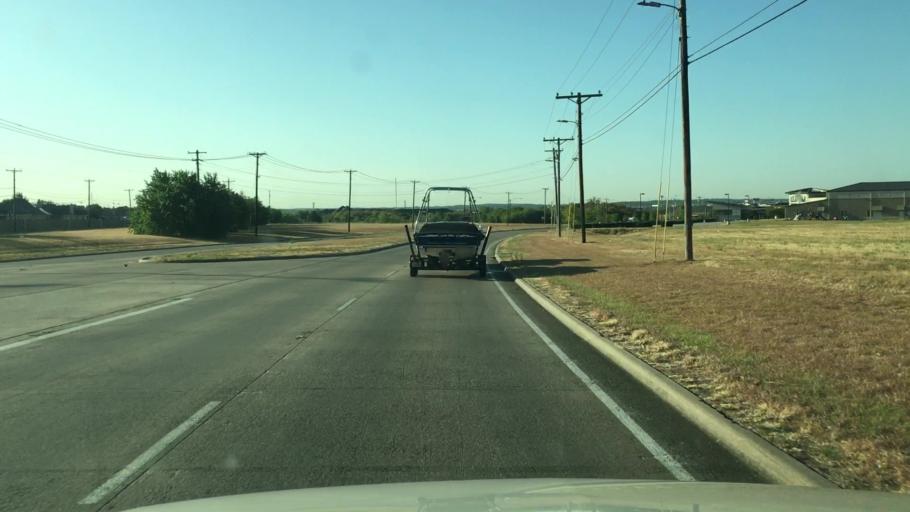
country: US
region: Texas
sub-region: Johnson County
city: Burleson
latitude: 32.5331
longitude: -97.3543
